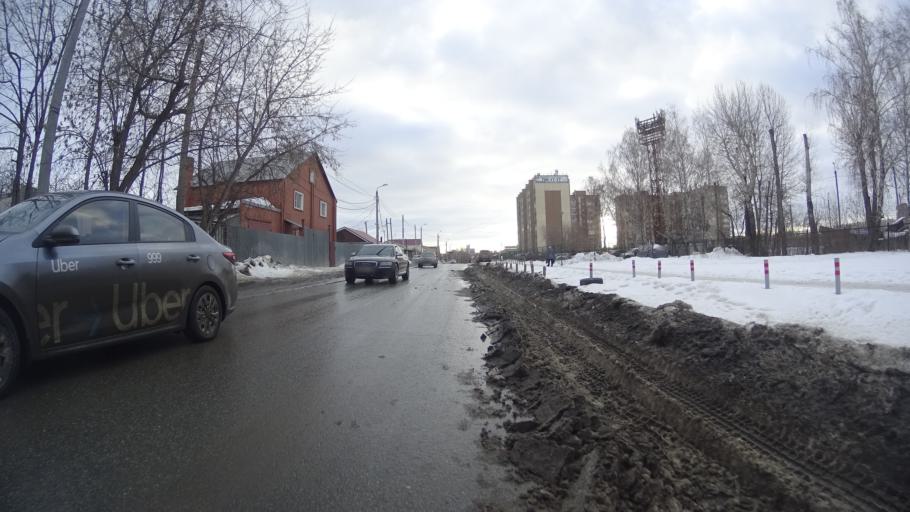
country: RU
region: Chelyabinsk
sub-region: Gorod Chelyabinsk
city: Chelyabinsk
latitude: 55.1393
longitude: 61.3963
